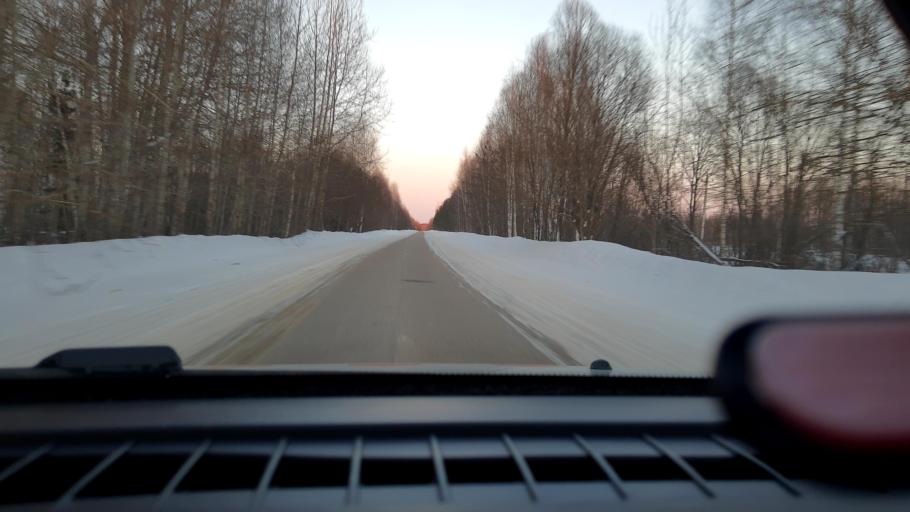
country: RU
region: Nizjnij Novgorod
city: Lyskovo
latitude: 56.1606
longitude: 45.1702
